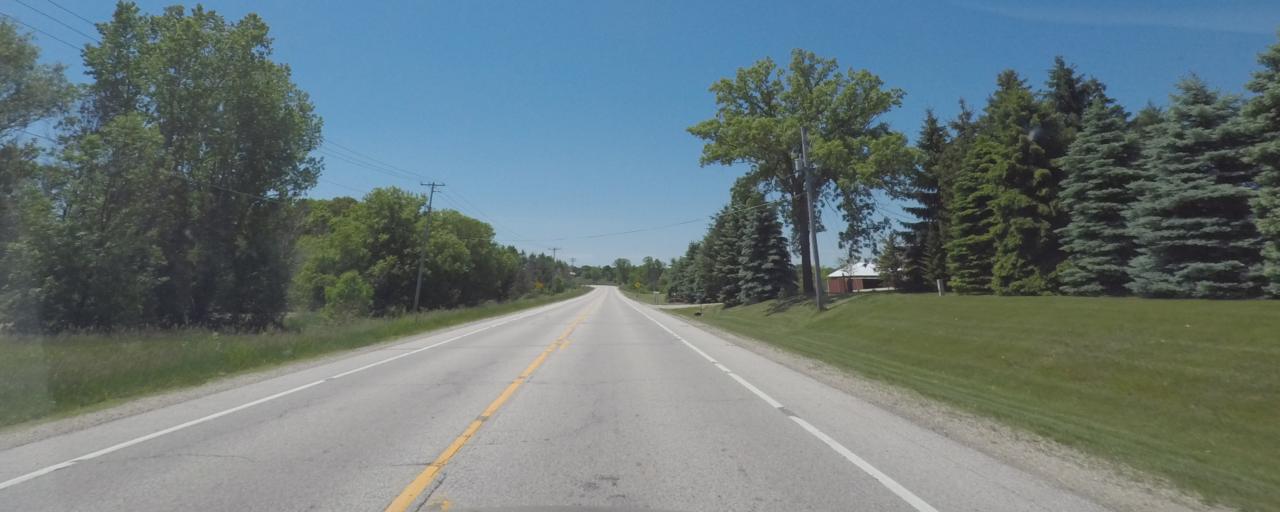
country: US
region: Wisconsin
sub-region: Ozaukee County
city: Kohler
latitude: 43.5448
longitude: -88.0821
